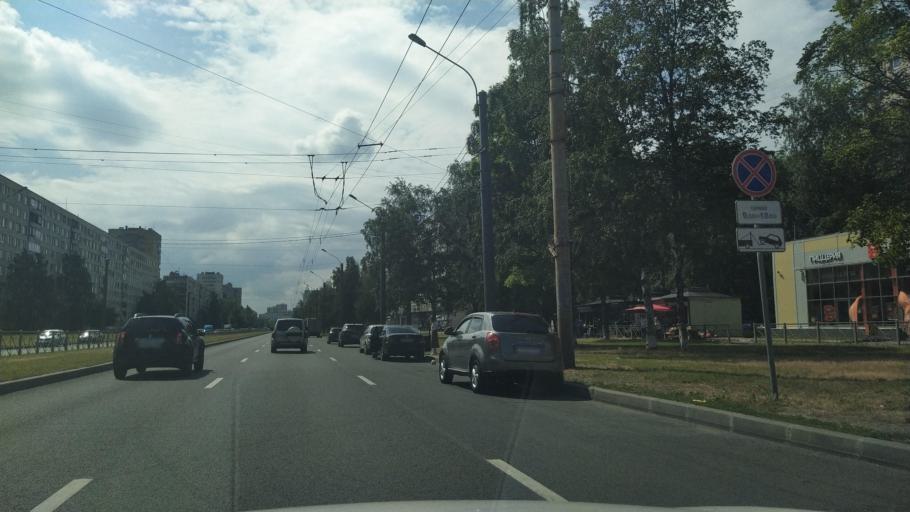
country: RU
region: Leningrad
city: Parnas
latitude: 60.0479
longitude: 30.3532
